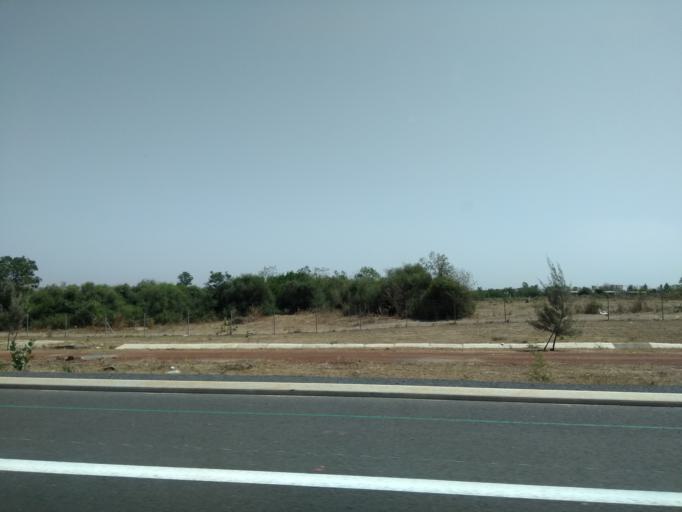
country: SN
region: Thies
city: Pout
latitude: 14.7351
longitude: -17.1713
